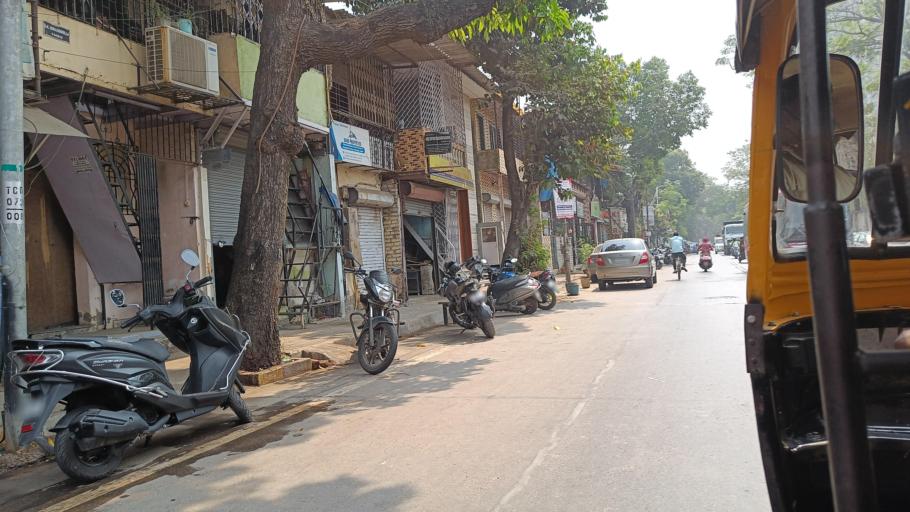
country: IN
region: Maharashtra
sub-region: Mumbai Suburban
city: Powai
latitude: 19.1544
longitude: 72.8380
